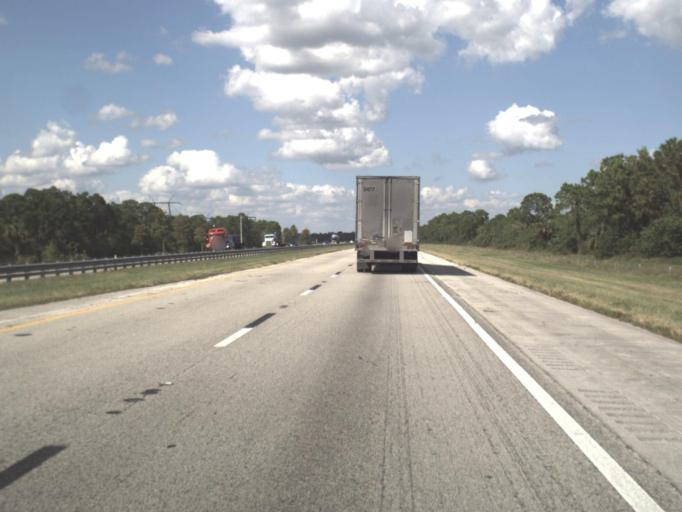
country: US
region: Florida
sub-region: Indian River County
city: West Vero Corridor
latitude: 27.5239
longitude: -80.6000
